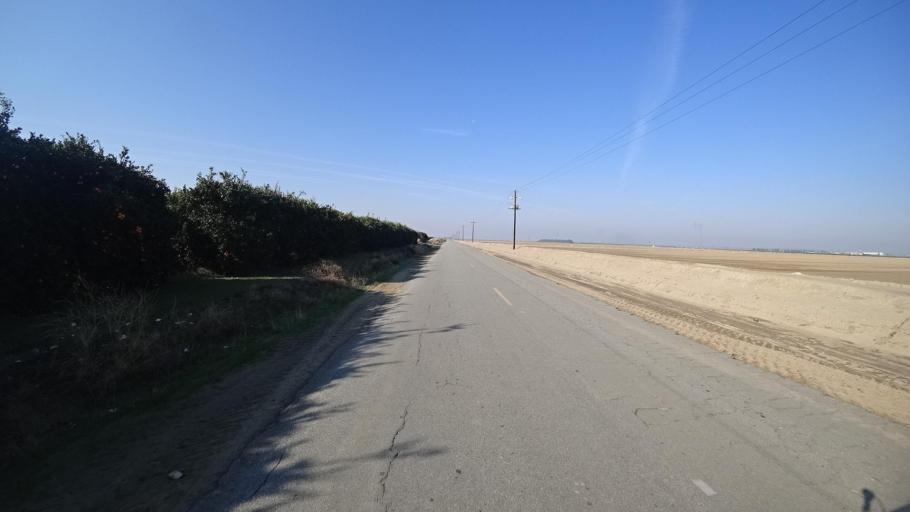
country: US
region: California
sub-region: Kern County
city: Weedpatch
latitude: 35.1217
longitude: -118.9343
